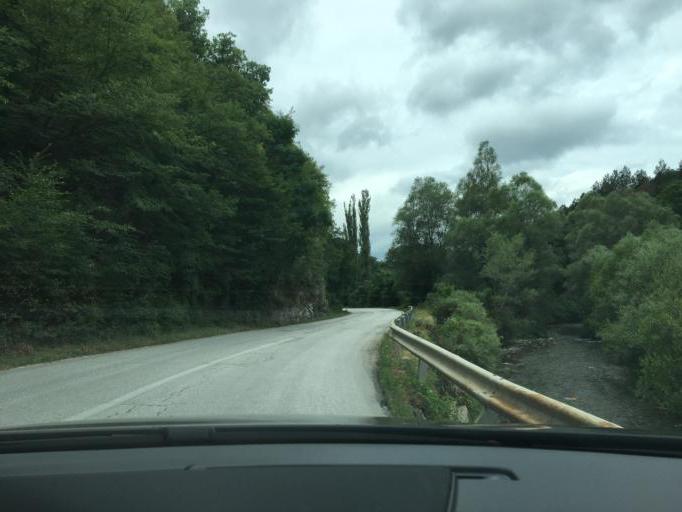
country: MK
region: Kriva Palanka
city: Kriva Palanka
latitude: 42.2203
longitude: 22.3555
